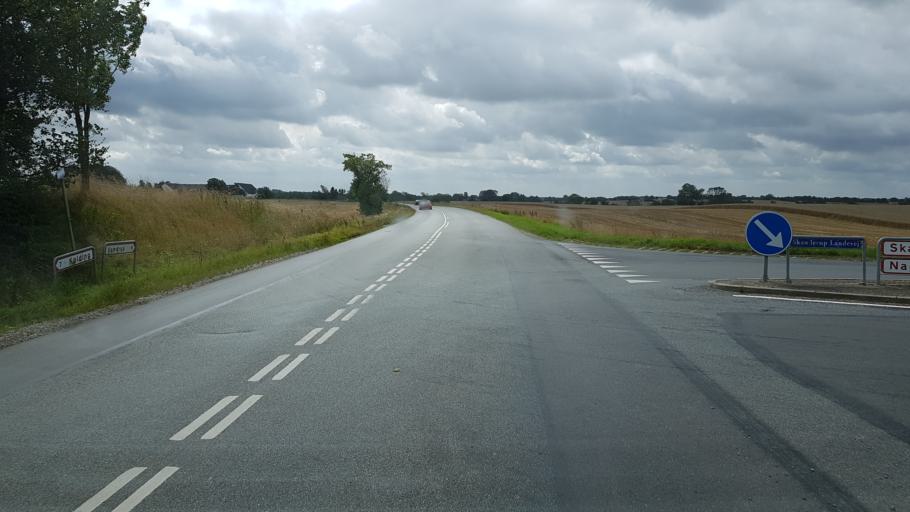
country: DK
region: South Denmark
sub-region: Kolding Kommune
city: Lunderskov
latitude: 55.4632
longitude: 9.3831
